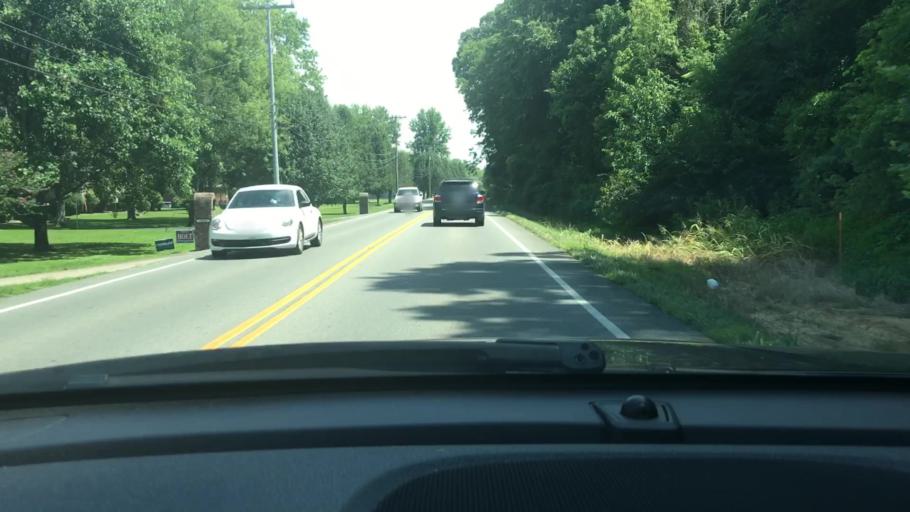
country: US
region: Tennessee
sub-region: Sumner County
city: Shackle Island
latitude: 36.3655
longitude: -86.6130
